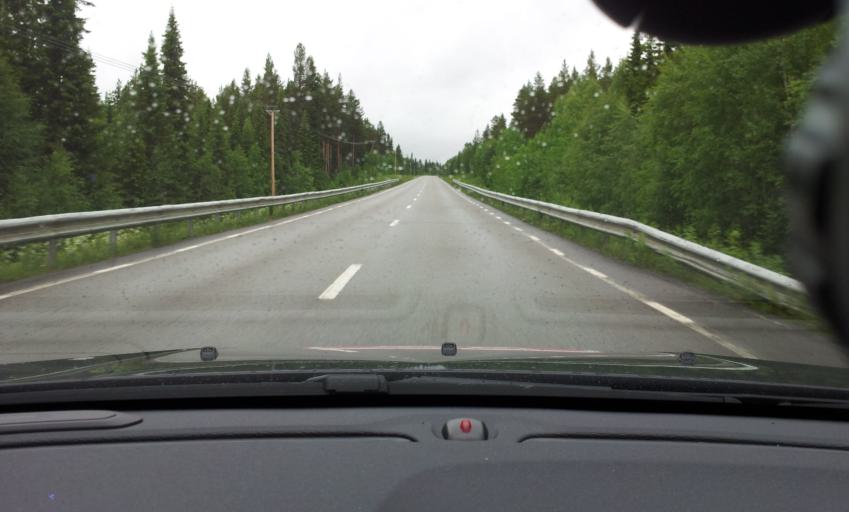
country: SE
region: Jaemtland
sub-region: Krokoms Kommun
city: Krokom
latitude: 63.4619
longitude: 14.4928
